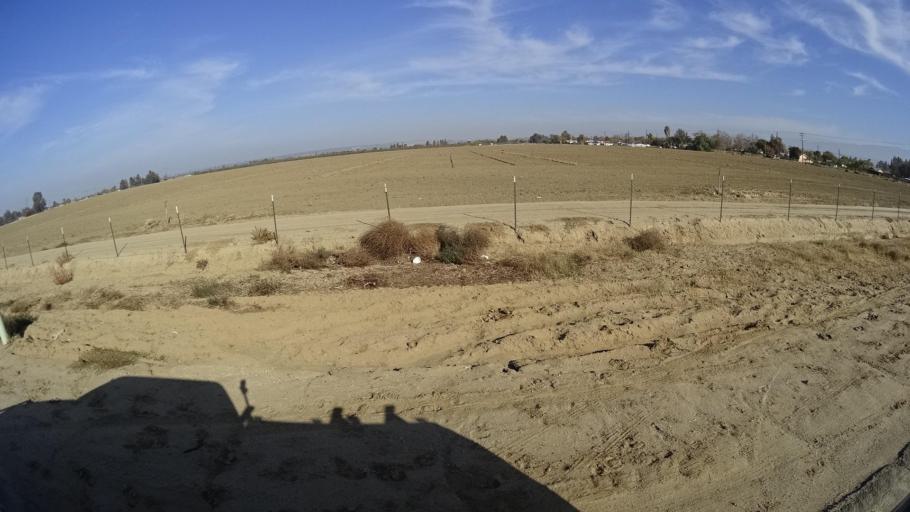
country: US
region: California
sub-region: Kern County
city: Lamont
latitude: 35.3249
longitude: -118.9162
